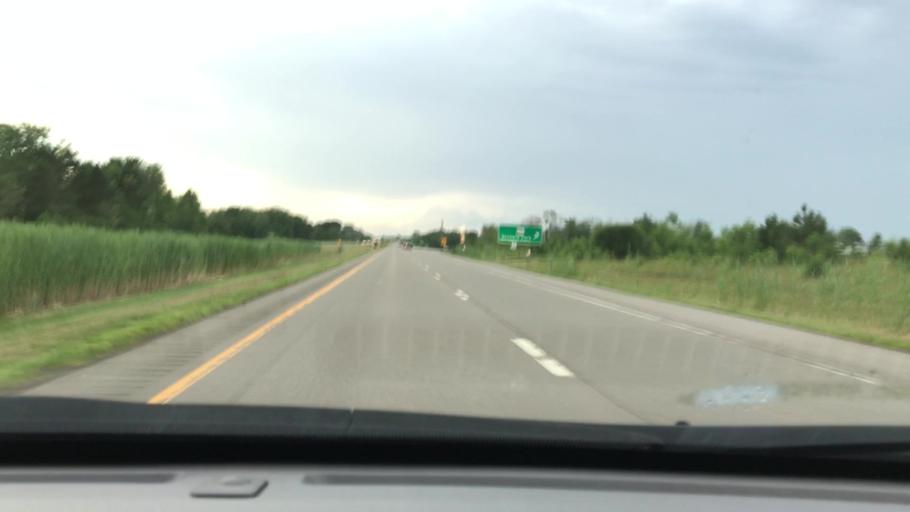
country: US
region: New York
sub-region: Erie County
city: Orchard Park
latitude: 42.7572
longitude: -78.7629
